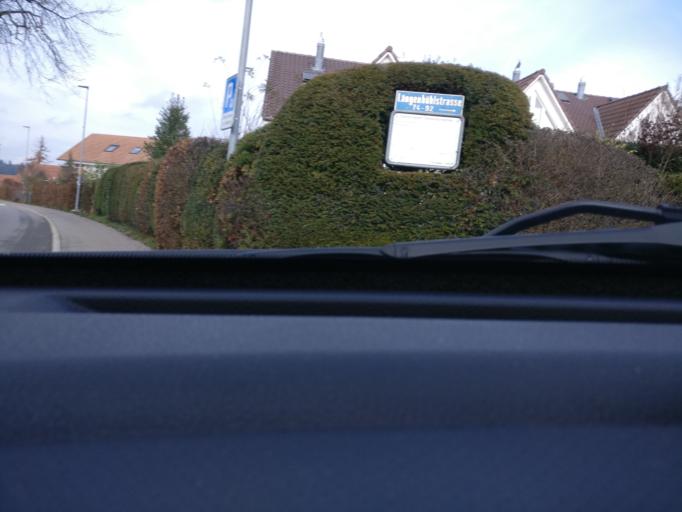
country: CH
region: Bern
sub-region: Bern-Mittelland District
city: Urtenen
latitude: 47.0113
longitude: 7.4839
